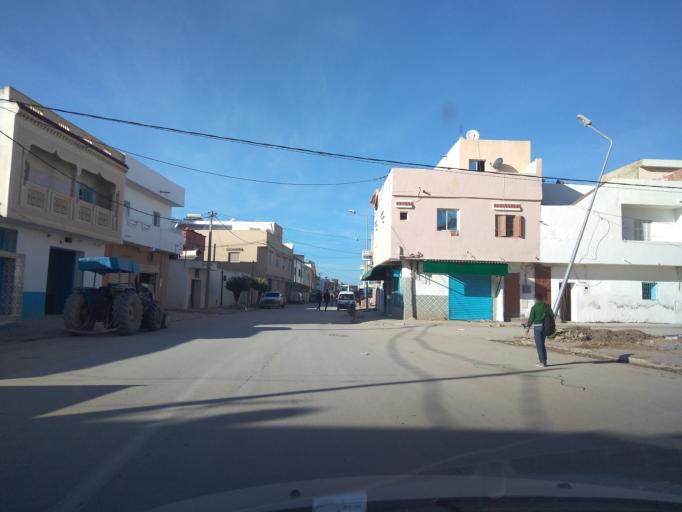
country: TN
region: Ariana
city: Qal'at al Andalus
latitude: 37.0606
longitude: 10.1190
